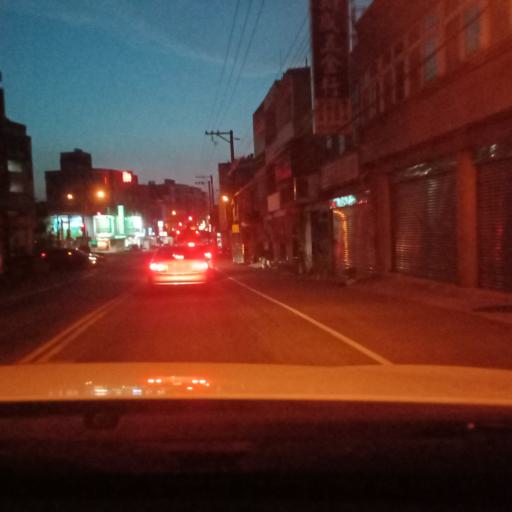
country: TW
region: Taiwan
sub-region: Hsinchu
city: Zhubei
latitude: 24.9019
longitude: 121.0500
